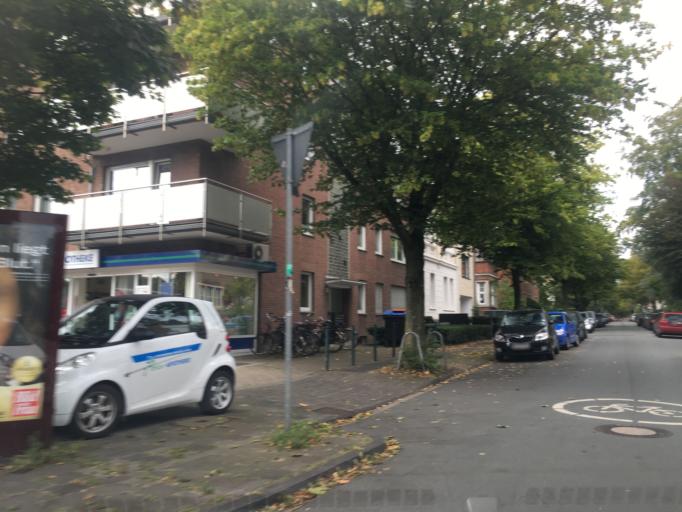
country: DE
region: North Rhine-Westphalia
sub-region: Regierungsbezirk Munster
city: Muenster
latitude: 51.9612
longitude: 7.6065
